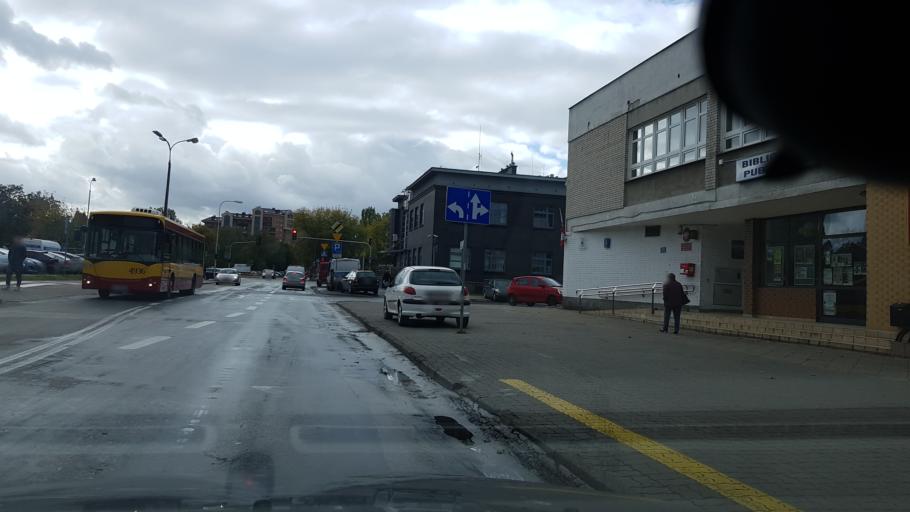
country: PL
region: Masovian Voivodeship
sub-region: Warszawa
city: Bielany
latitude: 52.2713
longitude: 20.9504
